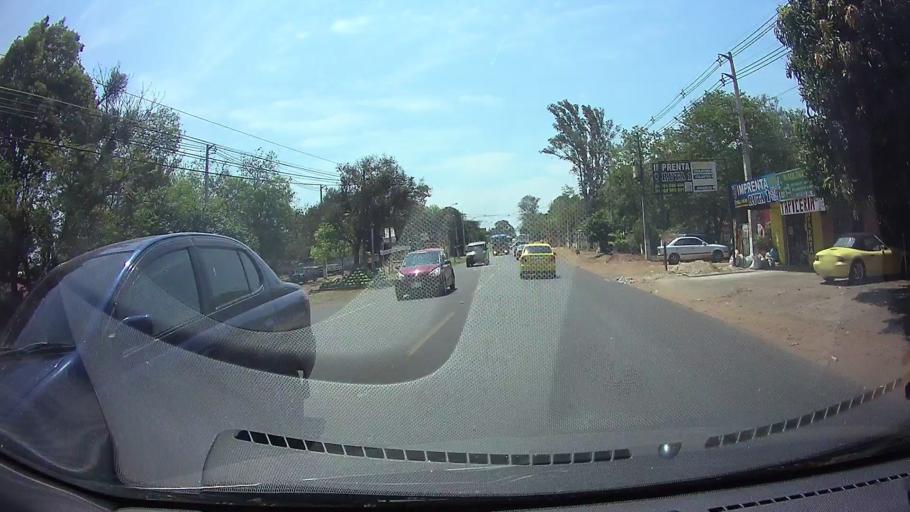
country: PY
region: Central
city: Capiata
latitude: -25.3877
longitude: -57.4710
